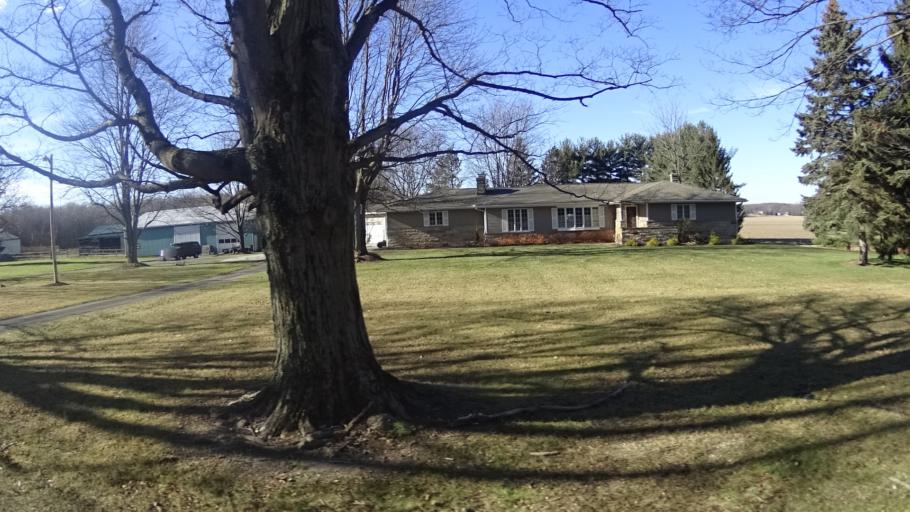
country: US
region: Ohio
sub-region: Lorain County
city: South Amherst
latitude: 41.3088
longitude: -82.2877
